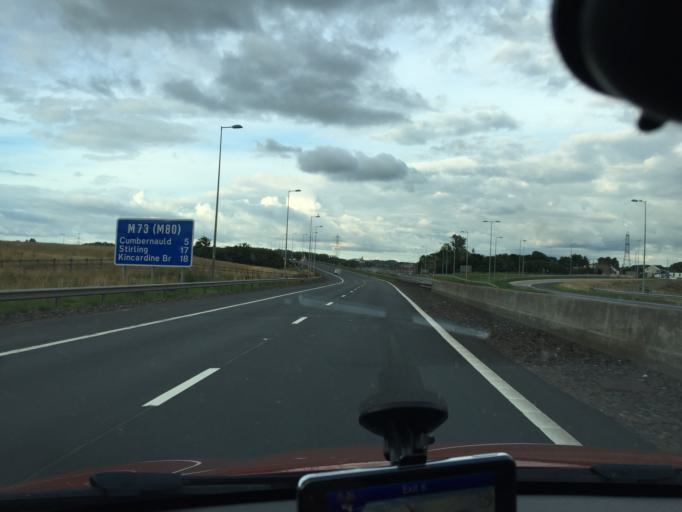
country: GB
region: Scotland
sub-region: North Lanarkshire
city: Glenboig
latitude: 55.9202
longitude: -4.0609
